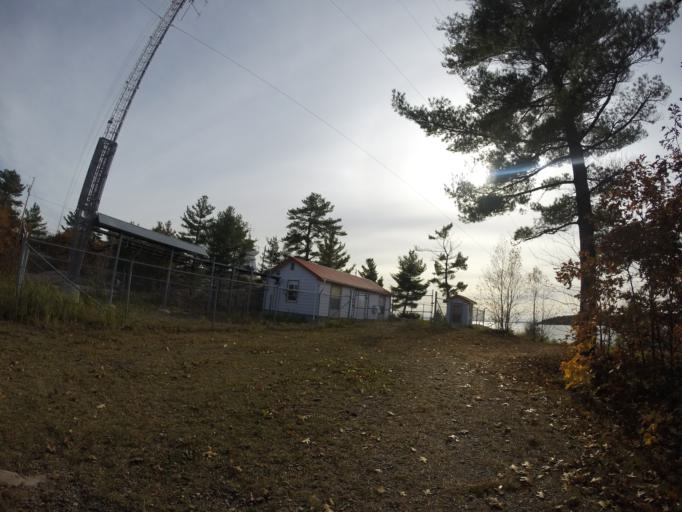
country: CA
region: Ontario
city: Espanola
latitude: 45.9688
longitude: -81.4889
